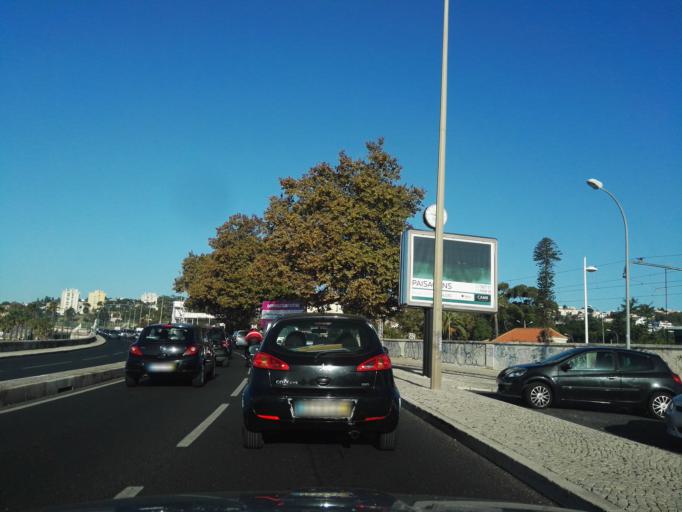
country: PT
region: Lisbon
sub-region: Oeiras
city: Terrugem
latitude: 38.6984
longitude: -9.2731
